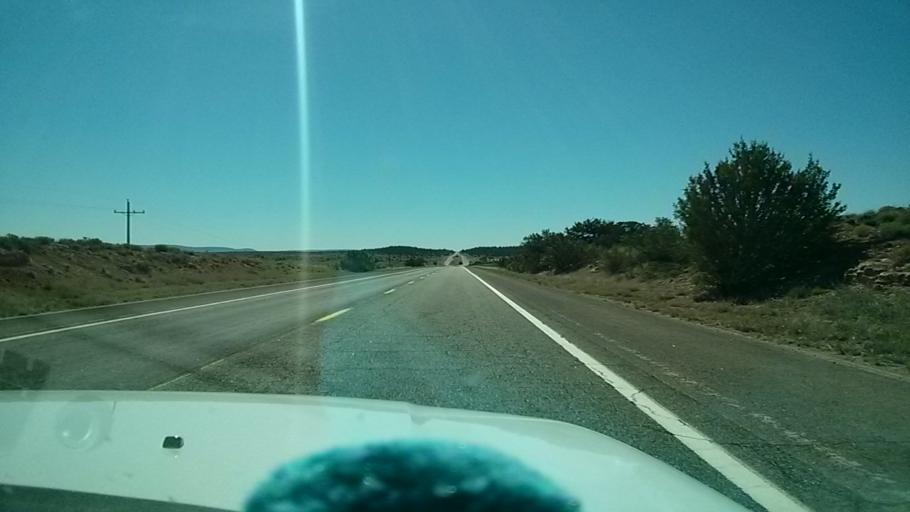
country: US
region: Arizona
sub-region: Mohave County
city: Peach Springs
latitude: 35.5347
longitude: -113.2480
